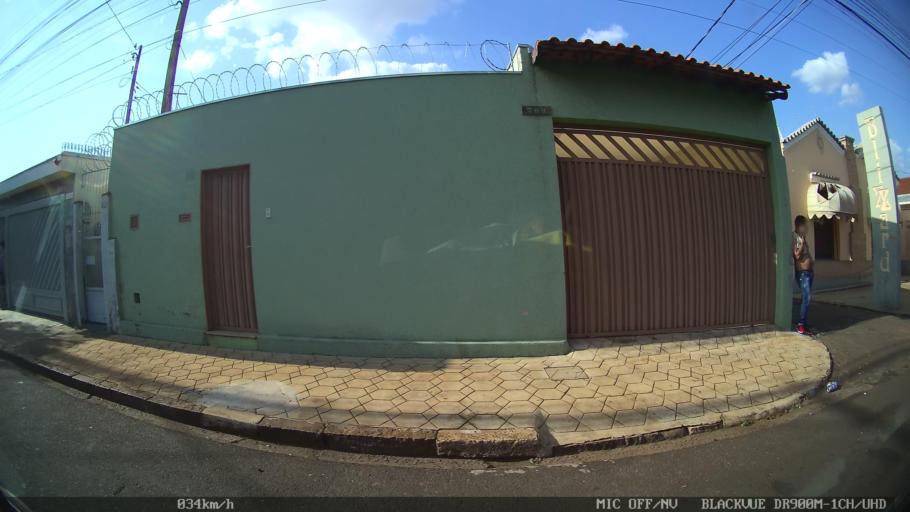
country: BR
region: Sao Paulo
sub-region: Ribeirao Preto
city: Ribeirao Preto
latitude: -21.1635
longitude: -47.8076
